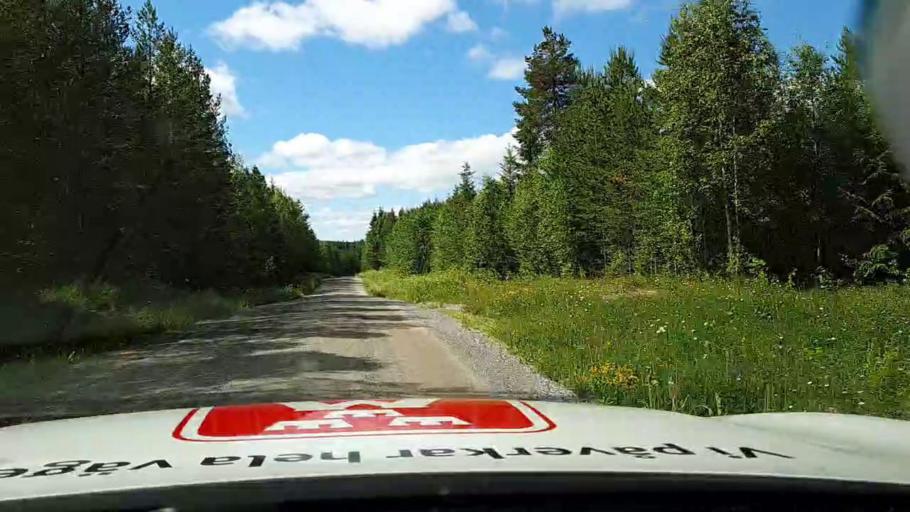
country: SE
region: Jaemtland
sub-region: Braecke Kommun
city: Braecke
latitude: 62.7379
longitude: 15.4896
